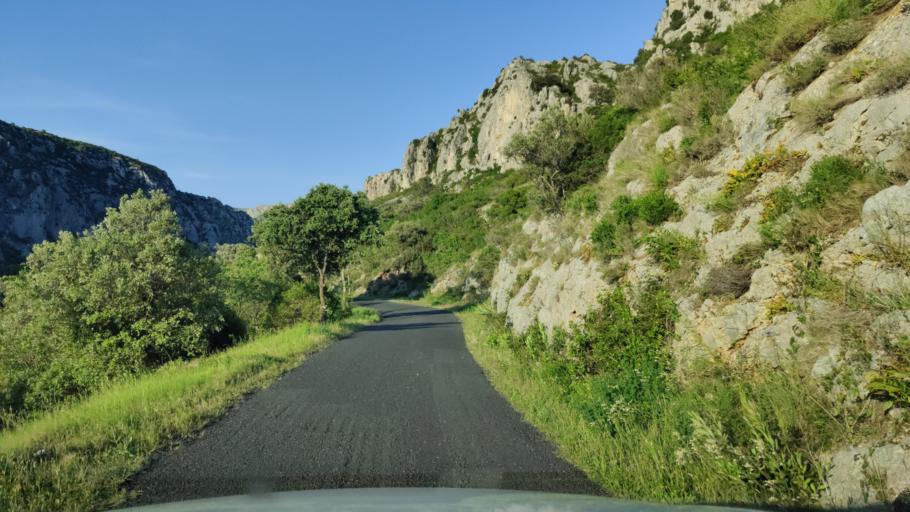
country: FR
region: Languedoc-Roussillon
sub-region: Departement des Pyrenees-Orientales
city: Estagel
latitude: 42.8033
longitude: 2.7343
